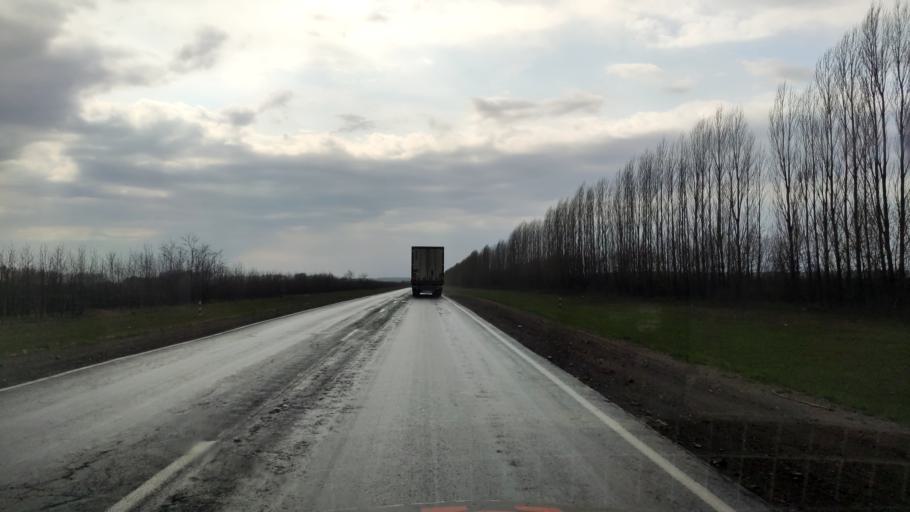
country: RU
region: Voronezj
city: Nizhnedevitsk
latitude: 51.5717
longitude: 38.2911
